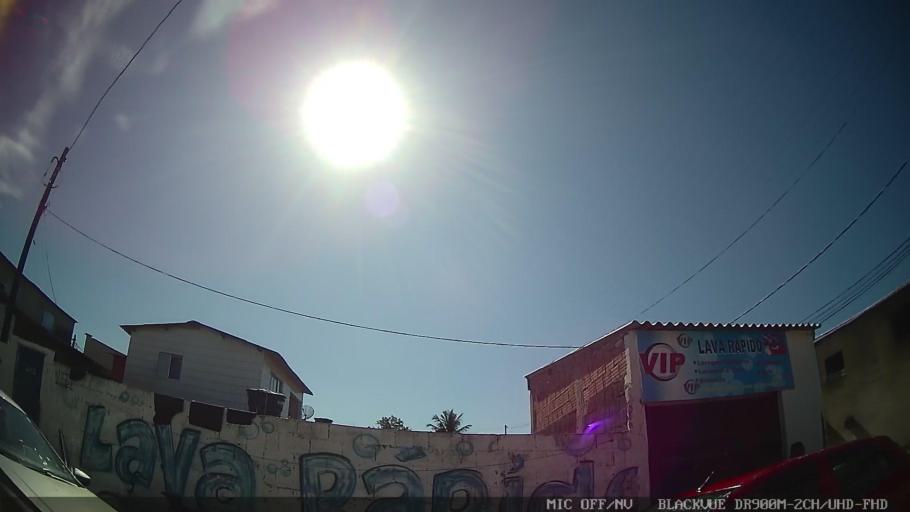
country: BR
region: Sao Paulo
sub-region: Santos
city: Santos
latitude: -23.9481
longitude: -46.2864
